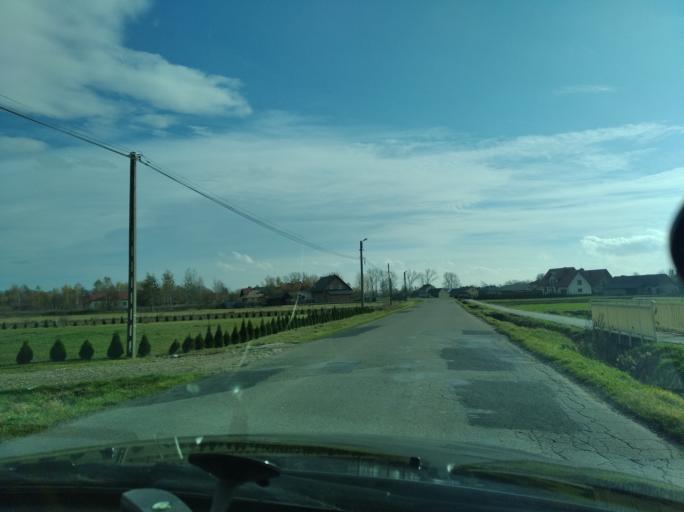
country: PL
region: Subcarpathian Voivodeship
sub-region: Powiat ropczycko-sedziszowski
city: Ostrow
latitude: 50.0971
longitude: 21.6368
